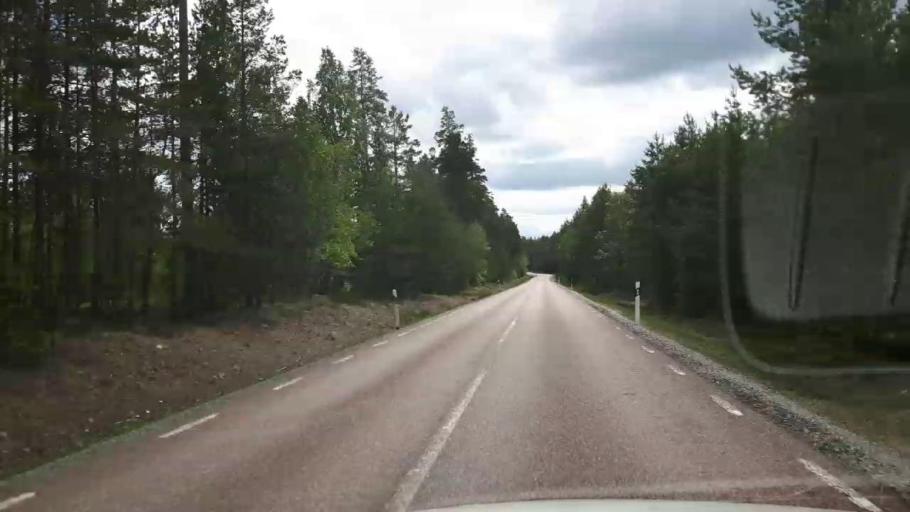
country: SE
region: Vaestmanland
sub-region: Fagersta Kommun
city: Fagersta
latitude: 59.8664
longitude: 15.8422
